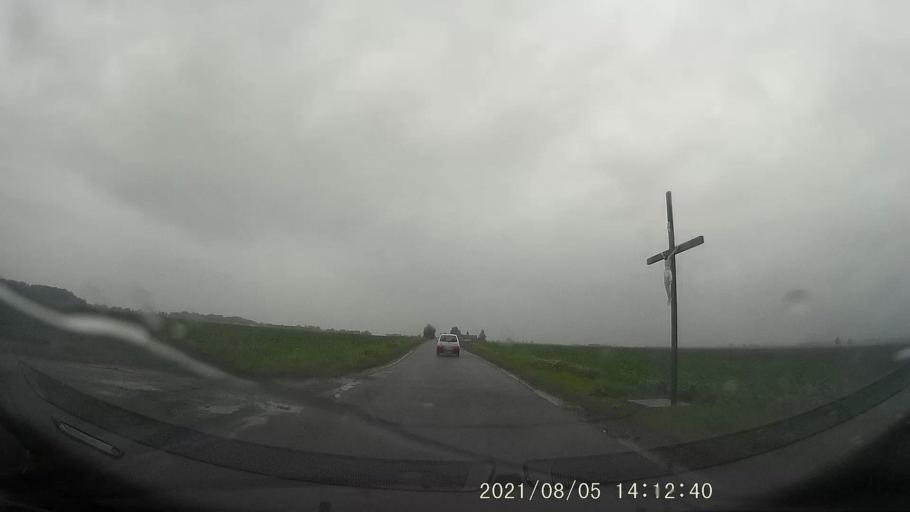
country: PL
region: Opole Voivodeship
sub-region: Powiat krapkowicki
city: Strzeleczki
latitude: 50.4685
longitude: 17.7581
